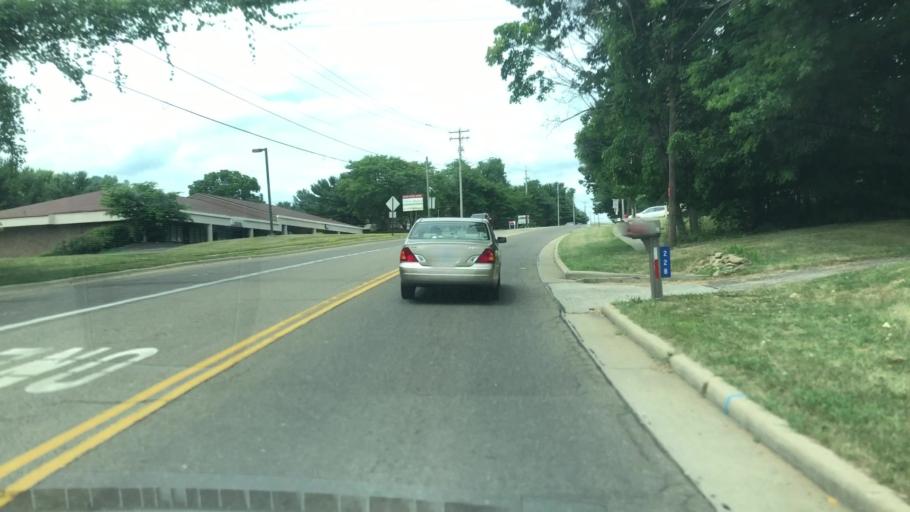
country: US
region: Ohio
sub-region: Summit County
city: Munroe Falls
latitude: 41.1457
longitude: -81.4403
